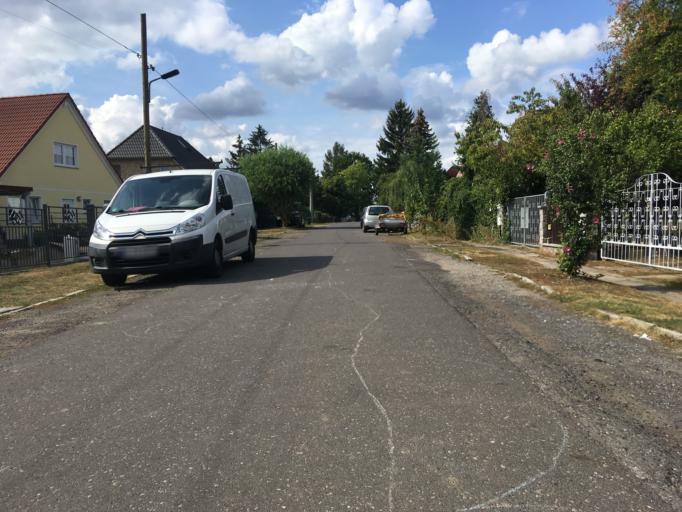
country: DE
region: Berlin
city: Karow
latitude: 52.6002
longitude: 13.4730
